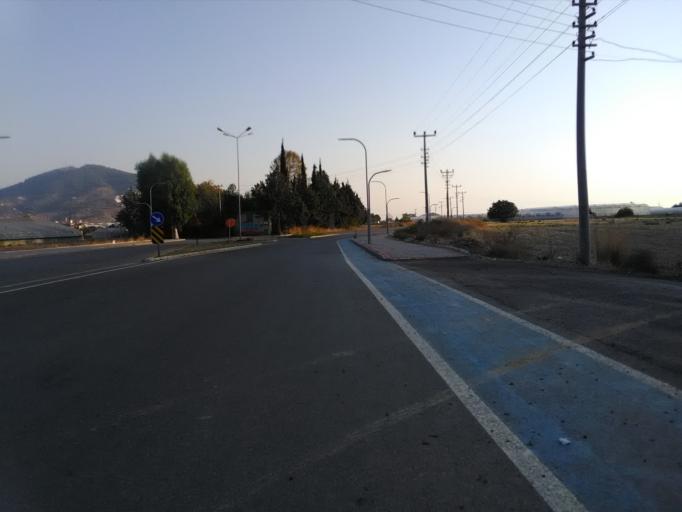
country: TR
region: Antalya
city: Gazipasa
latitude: 36.2597
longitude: 32.2903
